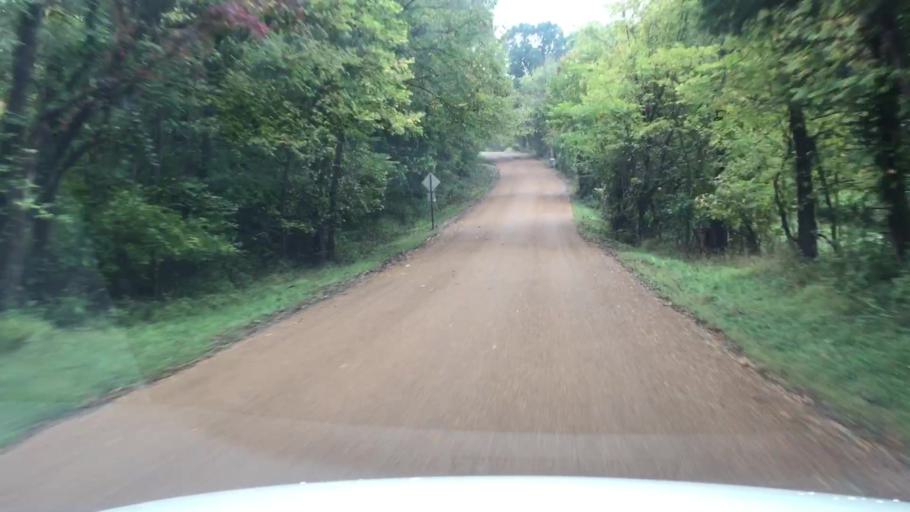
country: US
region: Missouri
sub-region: Boone County
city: Columbia
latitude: 38.8860
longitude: -92.4197
